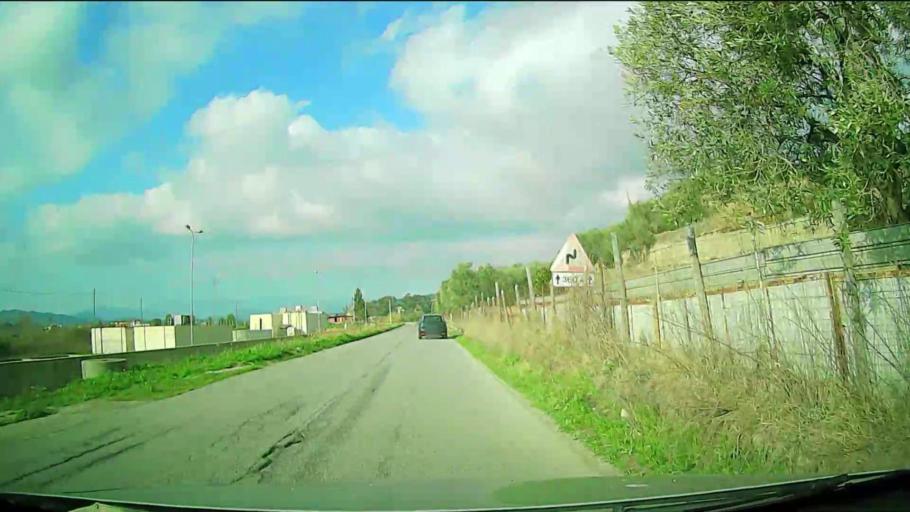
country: IT
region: Calabria
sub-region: Provincia di Crotone
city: Rocca di Neto
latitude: 39.1803
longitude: 17.0265
